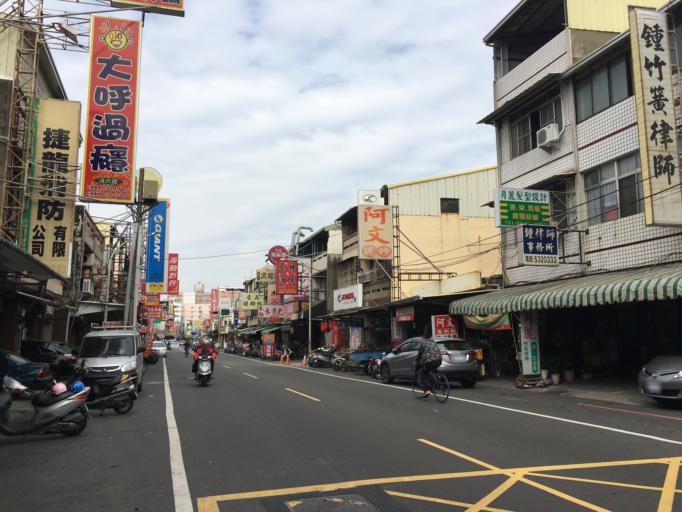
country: TW
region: Taiwan
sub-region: Yunlin
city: Douliu
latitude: 23.6992
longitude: 120.5382
